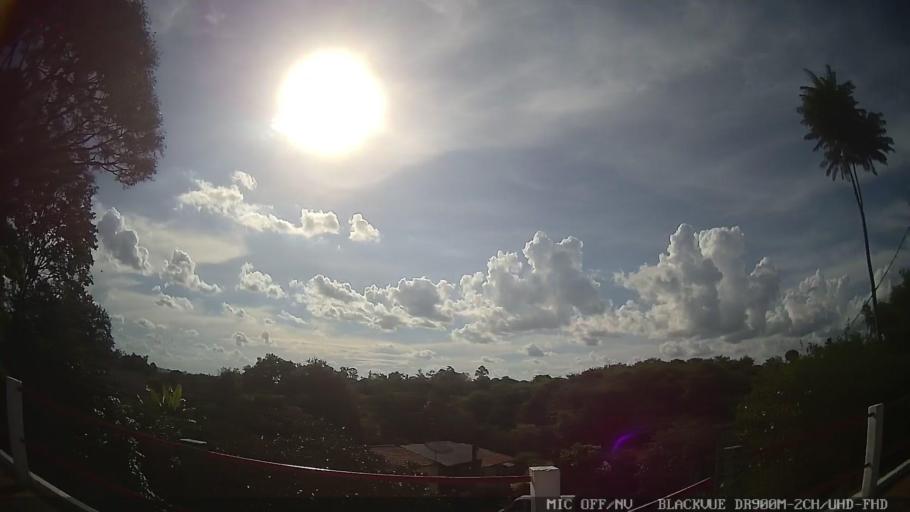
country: BR
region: Sao Paulo
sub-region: Laranjal Paulista
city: Laranjal Paulista
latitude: -23.0825
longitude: -47.7915
